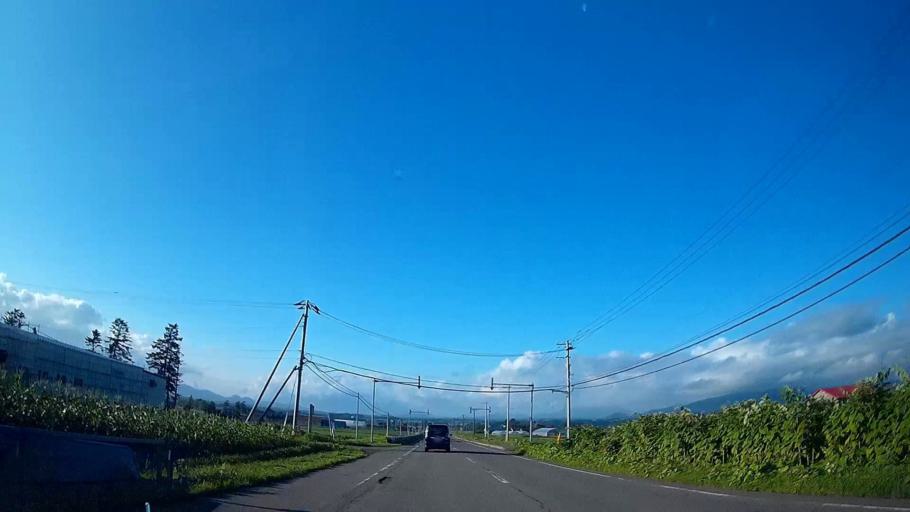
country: JP
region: Hokkaido
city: Date
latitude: 42.6305
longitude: 140.8001
